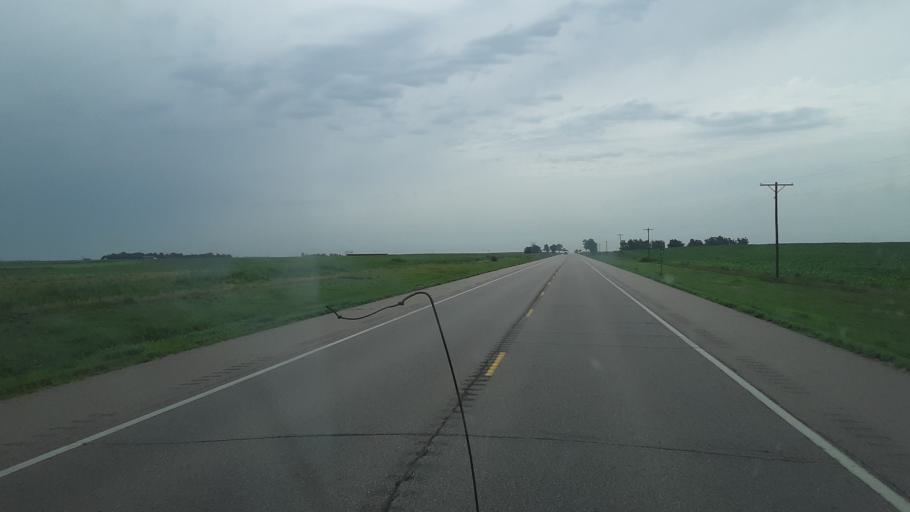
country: US
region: Kansas
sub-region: Stafford County
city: Saint John
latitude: 37.9563
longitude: -98.9434
